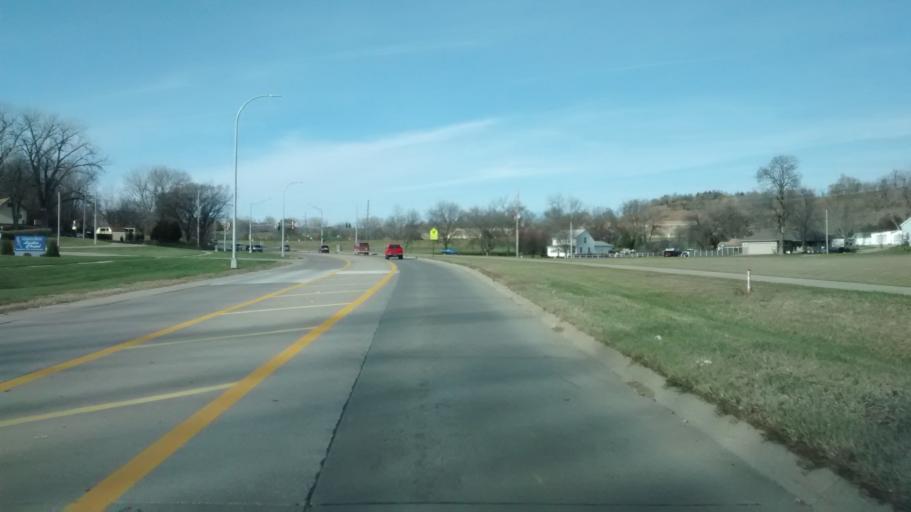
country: US
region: Iowa
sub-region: Woodbury County
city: Sioux City
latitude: 42.5396
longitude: -96.3786
